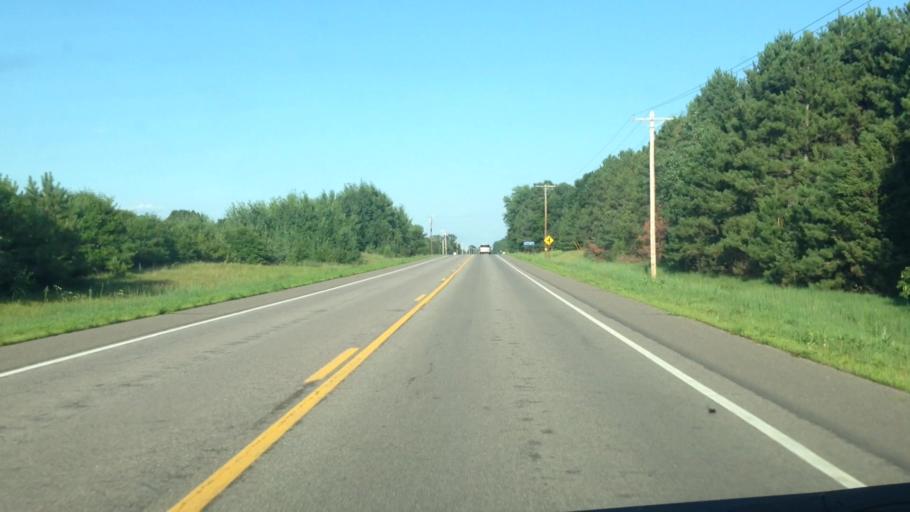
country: US
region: Minnesota
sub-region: Sherburne County
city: Big Lake
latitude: 45.4477
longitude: -93.7298
